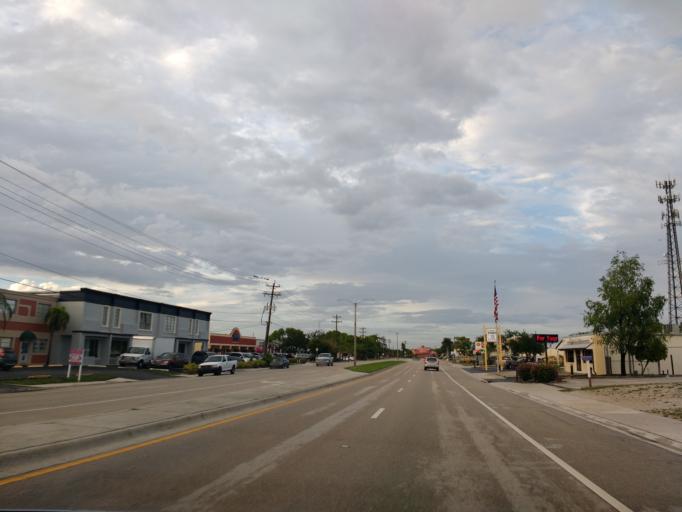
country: US
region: Florida
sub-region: Lee County
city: Lochmoor Waterway Estates
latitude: 26.6337
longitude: -81.9525
